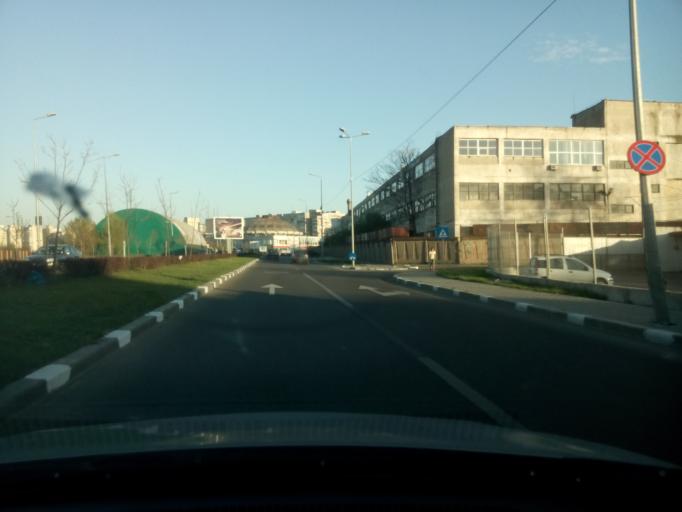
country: RO
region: Ilfov
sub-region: Comuna Fundeni-Dobroesti
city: Fundeni
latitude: 44.4472
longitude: 26.1544
